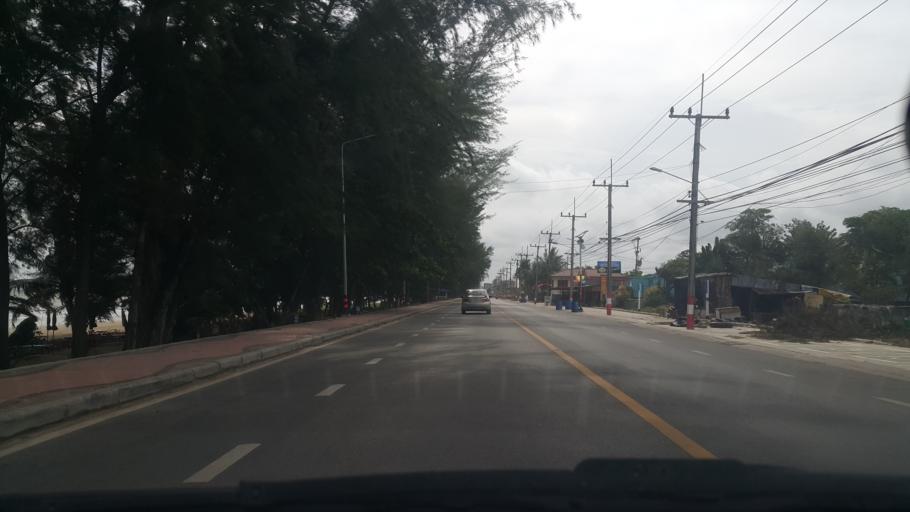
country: TH
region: Rayong
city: Rayong
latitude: 12.6237
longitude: 101.3604
